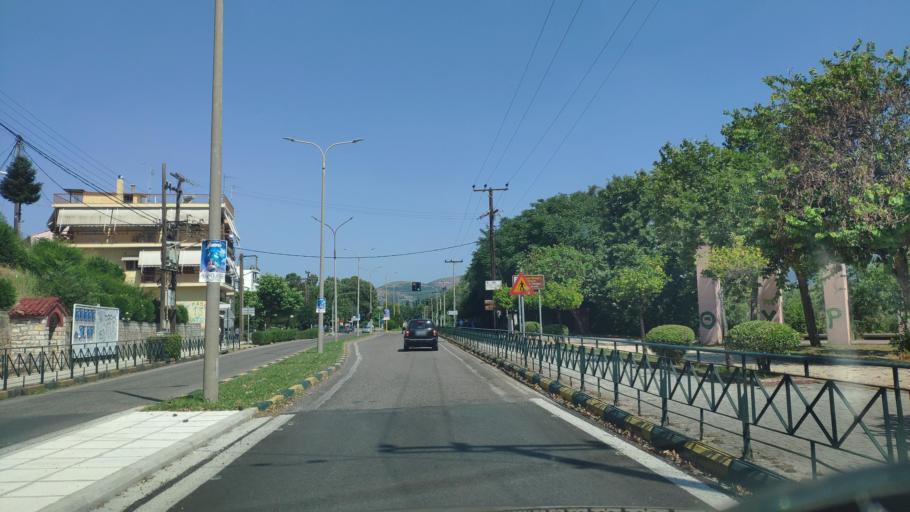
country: GR
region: Epirus
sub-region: Nomos Artas
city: Arta
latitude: 39.1626
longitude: 20.9927
